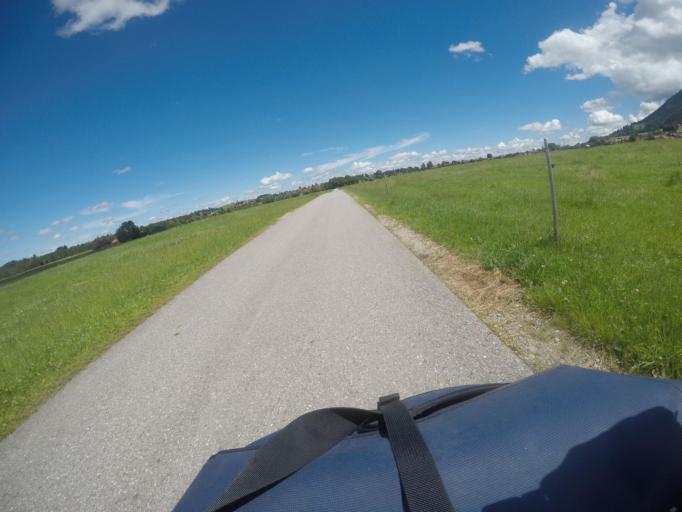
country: DE
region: Bavaria
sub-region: Swabia
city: Halblech
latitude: 47.6145
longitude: 10.7986
